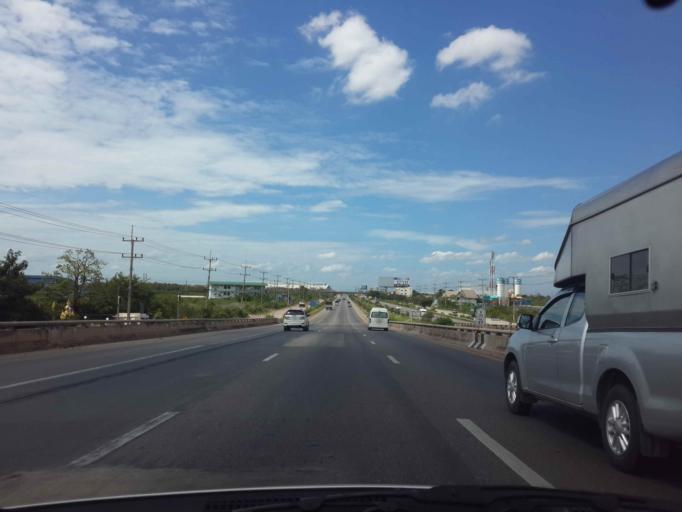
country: TH
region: Samut Sakhon
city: Ban Phaeo
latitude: 13.4869
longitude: 100.1211
